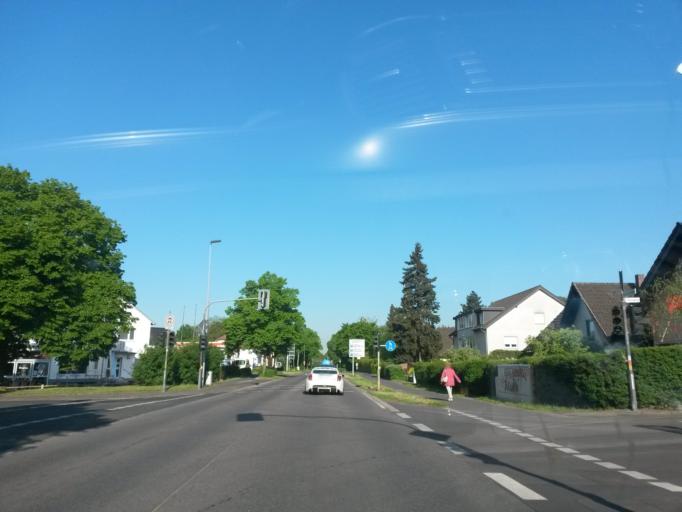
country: DE
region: North Rhine-Westphalia
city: Sankt Augustin
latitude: 50.7725
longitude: 7.1909
